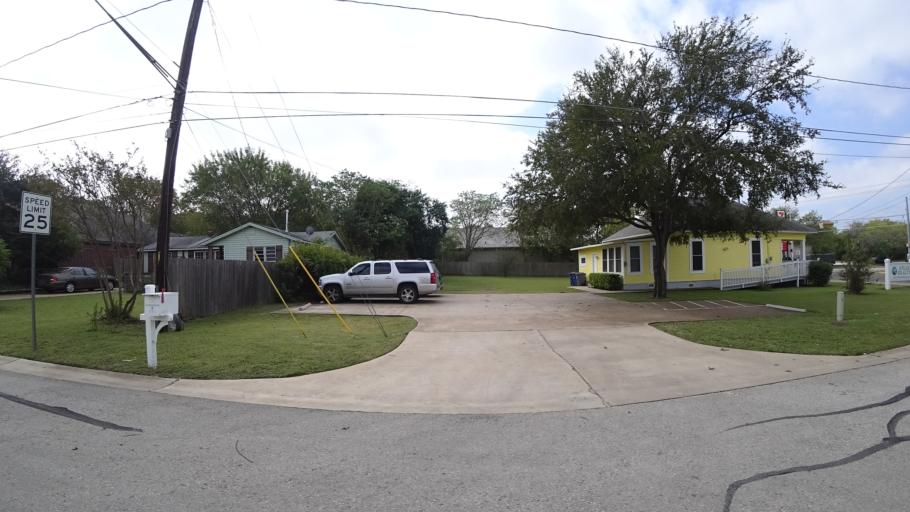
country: US
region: Texas
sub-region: Travis County
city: Shady Hollow
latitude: 30.2032
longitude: -97.8367
